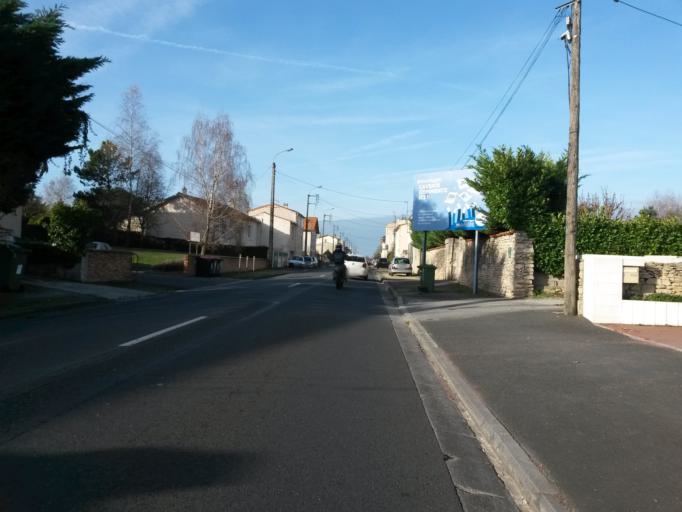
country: FR
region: Poitou-Charentes
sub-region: Departement des Deux-Sevres
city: Aiffres
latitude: 46.3171
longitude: -0.4300
